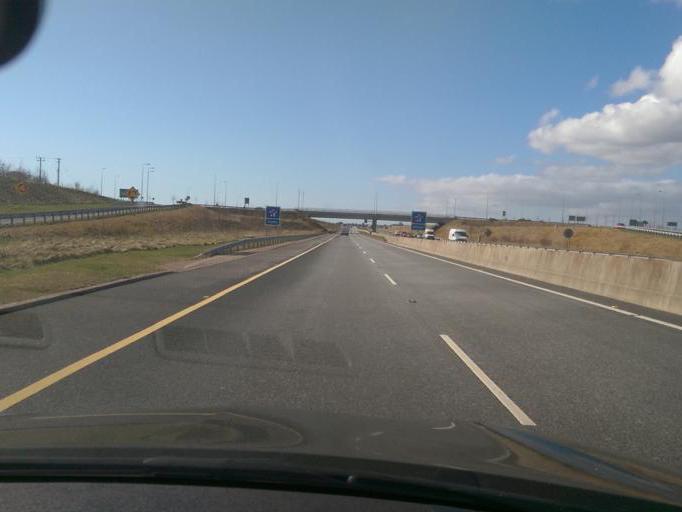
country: IE
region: Connaught
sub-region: County Galway
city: Oranmore
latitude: 53.2953
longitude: -8.9203
